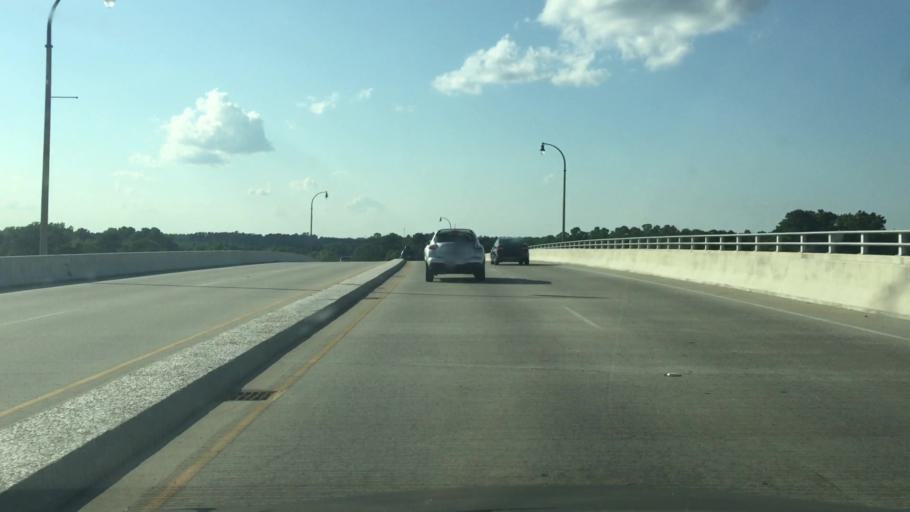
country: US
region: South Carolina
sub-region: Horry County
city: North Myrtle Beach
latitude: 33.8338
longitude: -78.6841
